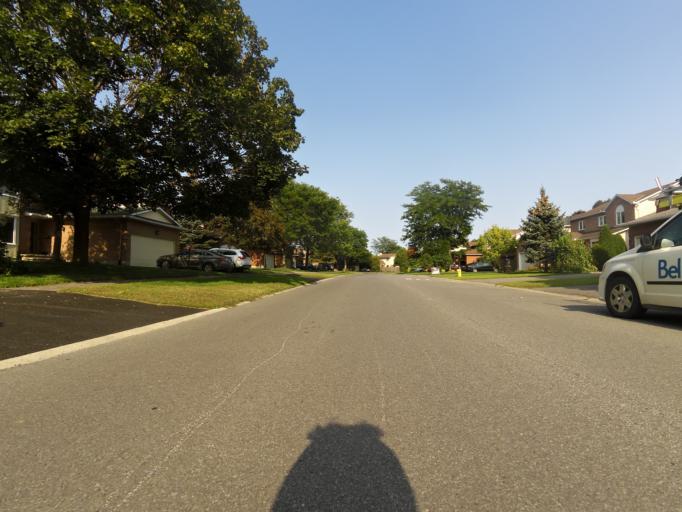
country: CA
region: Ontario
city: Bells Corners
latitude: 45.2973
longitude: -75.8703
